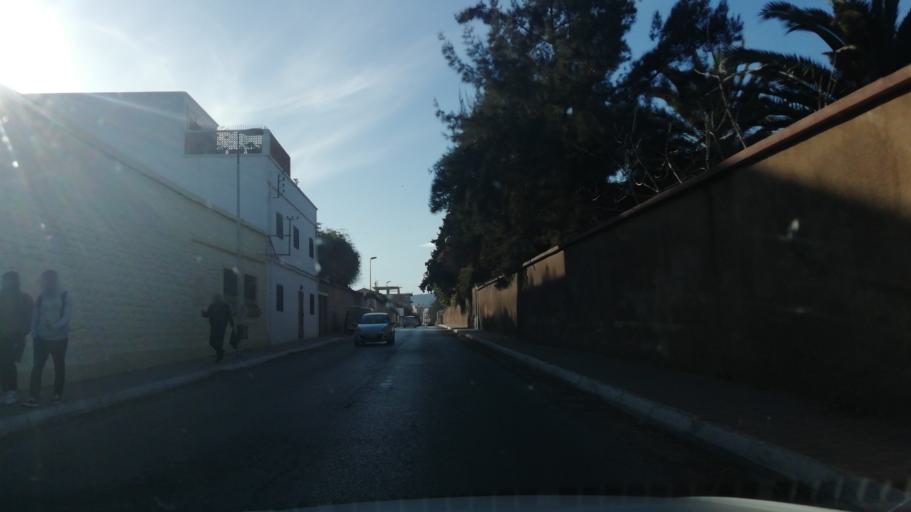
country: DZ
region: Oran
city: Oran
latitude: 35.6933
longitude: -0.6400
